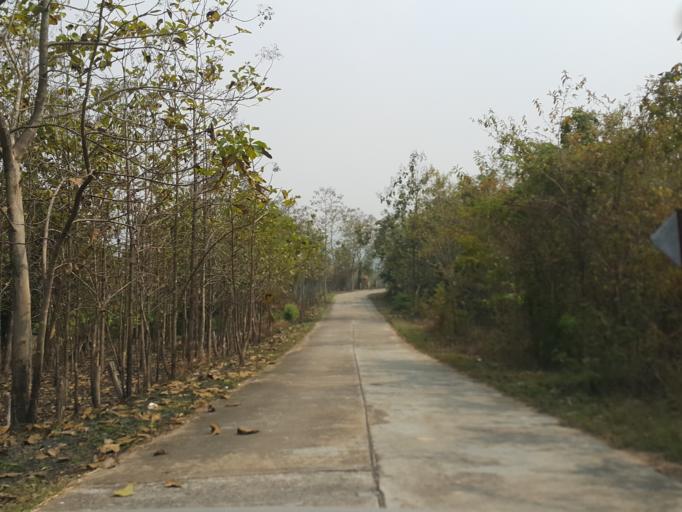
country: TH
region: Lampang
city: Thoen
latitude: 17.6346
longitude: 99.2557
